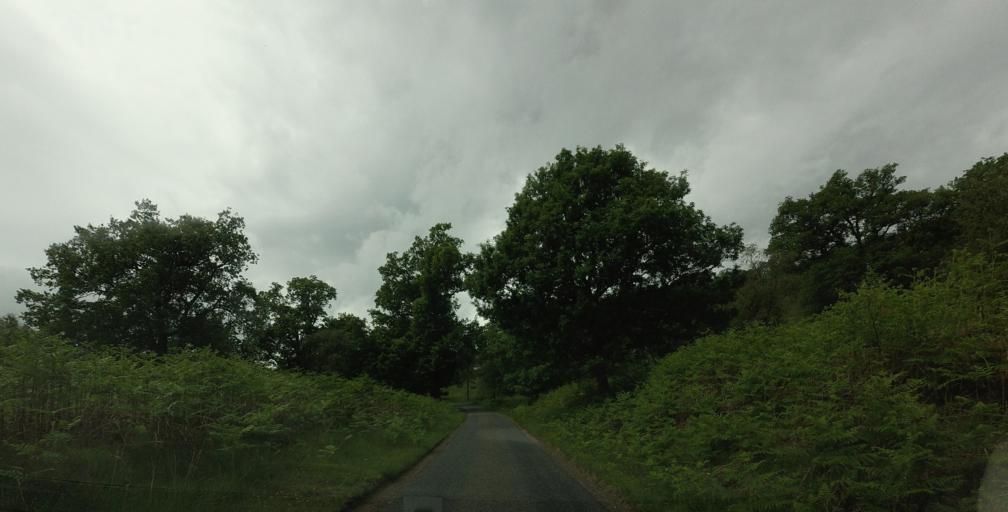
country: GB
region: Scotland
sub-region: Highland
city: Fort William
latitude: 56.7752
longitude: -5.2109
